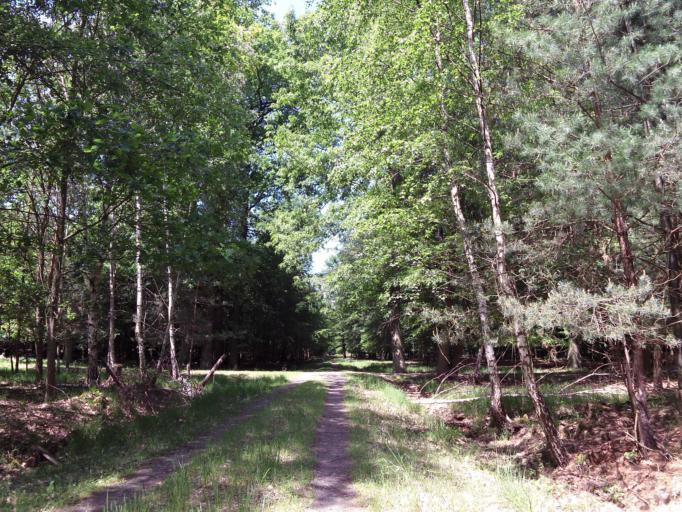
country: DE
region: Hesse
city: Kelsterbach
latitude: 50.0122
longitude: 8.5337
